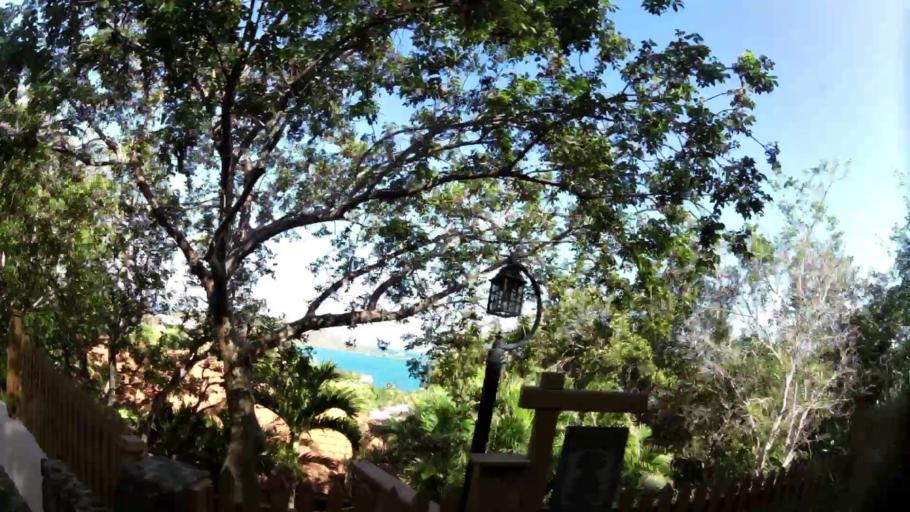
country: VG
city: Tortola
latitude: 18.4959
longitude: -64.3838
